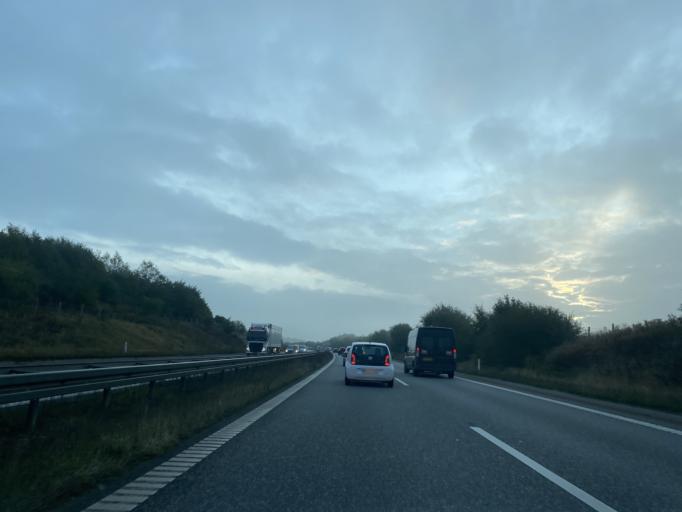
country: DK
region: Central Jutland
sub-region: Skanderborg Kommune
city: Skovby
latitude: 56.1421
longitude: 9.9439
